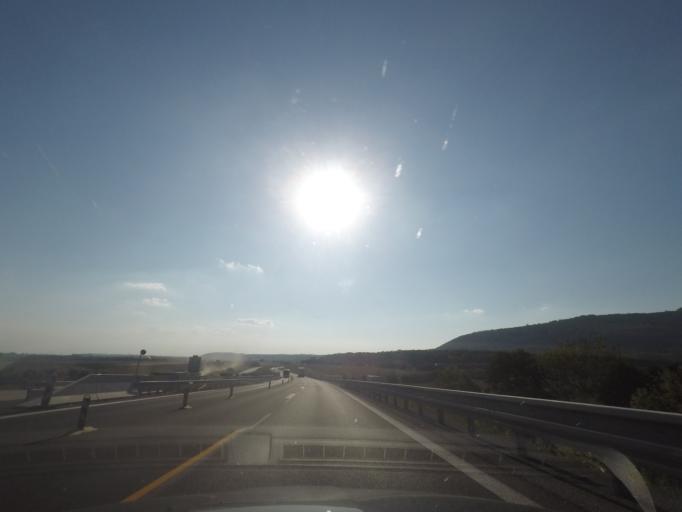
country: CZ
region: Olomoucky
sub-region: Okres Prerov
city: Lipnik nad Becvou
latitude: 49.5478
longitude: 17.5714
